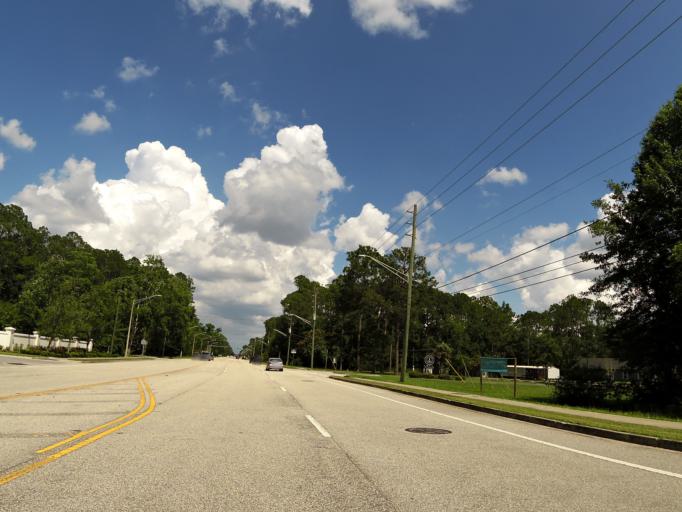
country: US
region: Florida
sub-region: Saint Johns County
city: Fruit Cove
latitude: 30.1492
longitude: -81.5777
